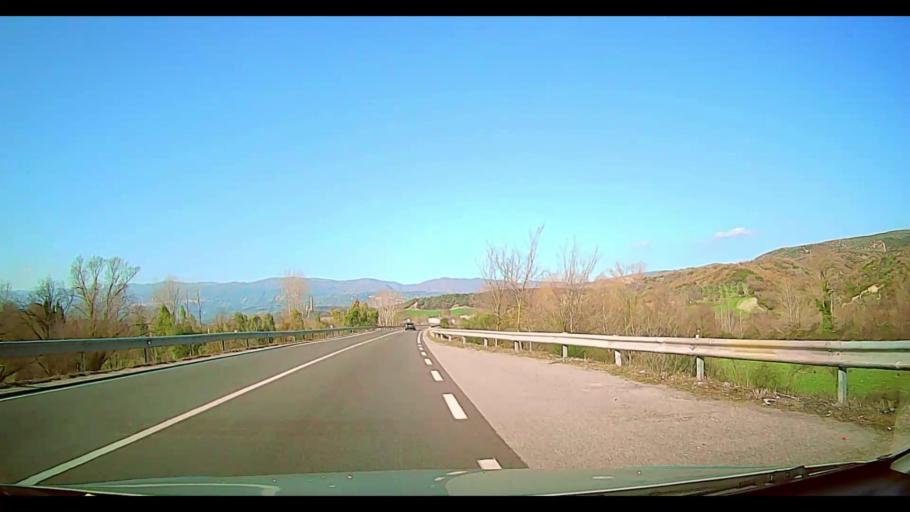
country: IT
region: Calabria
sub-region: Provincia di Crotone
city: Belvedere Spinello
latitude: 39.1879
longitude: 16.8561
